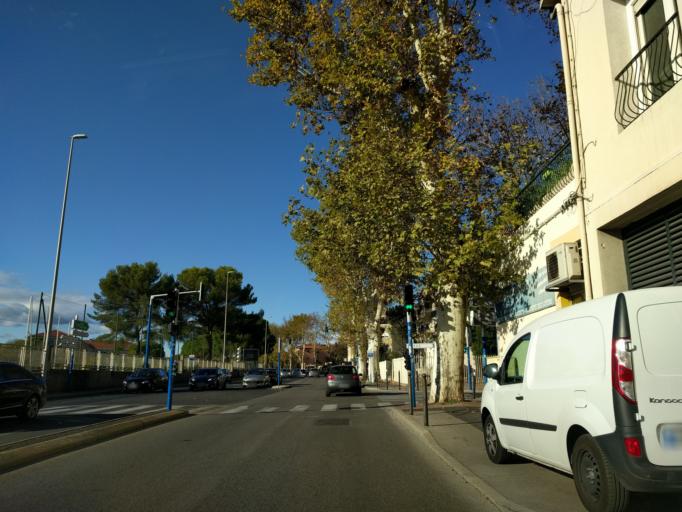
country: FR
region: Languedoc-Roussillon
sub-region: Departement de l'Herault
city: Montpellier
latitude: 43.6218
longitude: 3.8643
